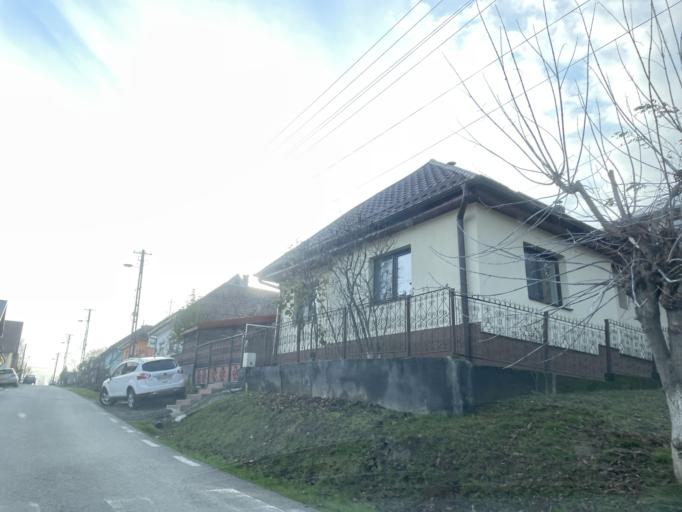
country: RO
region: Mures
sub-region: Municipiul Reghin
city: Reghin
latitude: 46.7821
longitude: 24.6931
